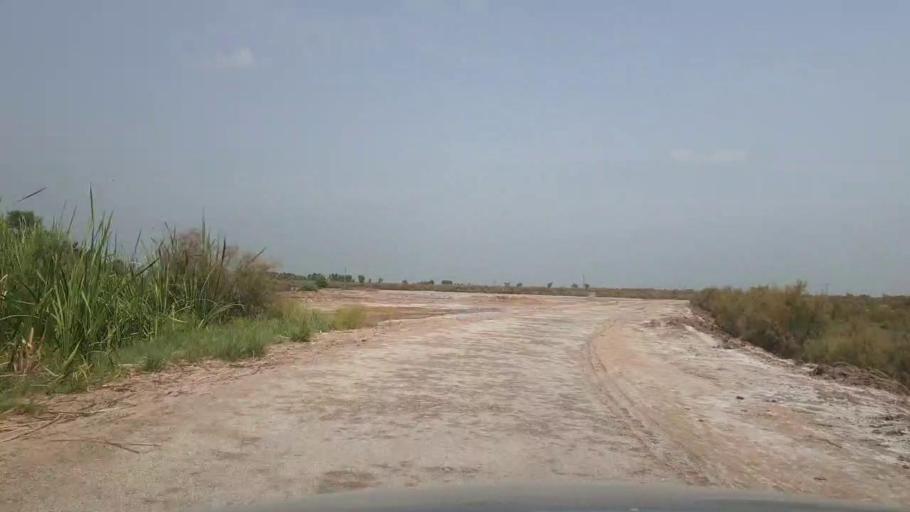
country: PK
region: Sindh
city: Garhi Yasin
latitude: 27.9514
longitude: 68.3651
